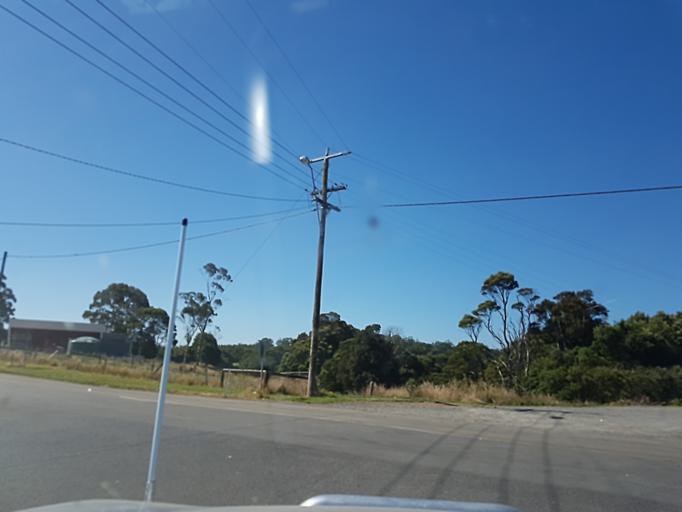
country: AU
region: Victoria
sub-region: Colac-Otway
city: Apollo Bay
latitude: -38.6799
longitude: 143.3911
